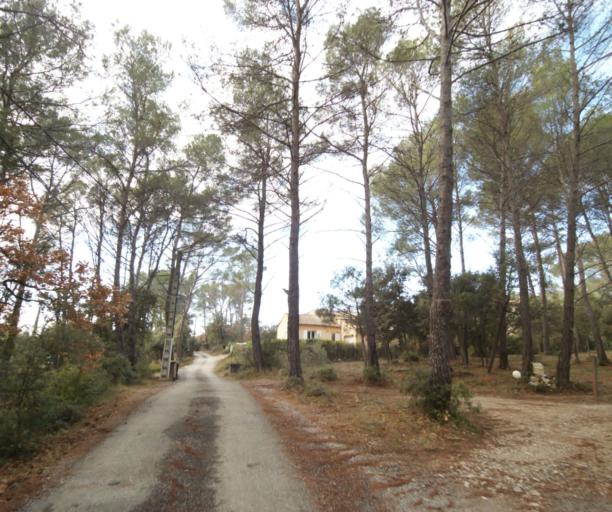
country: FR
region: Provence-Alpes-Cote d'Azur
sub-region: Departement du Var
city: Trans-en-Provence
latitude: 43.4872
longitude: 6.5001
